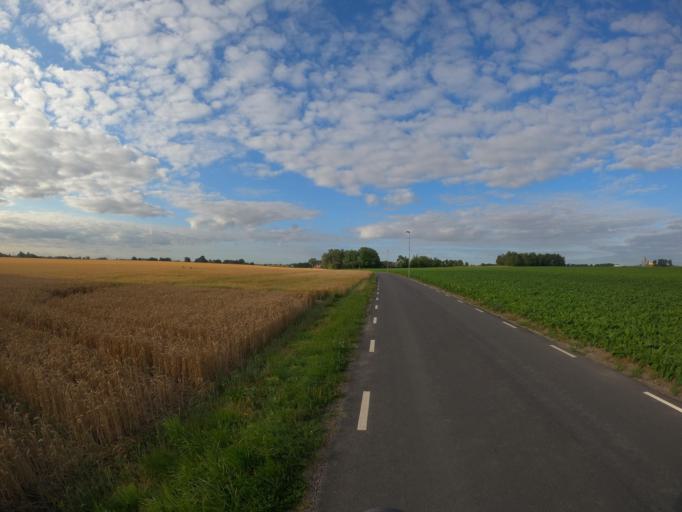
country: SE
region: Skane
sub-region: Staffanstorps Kommun
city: Staffanstorp
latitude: 55.6731
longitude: 13.2014
